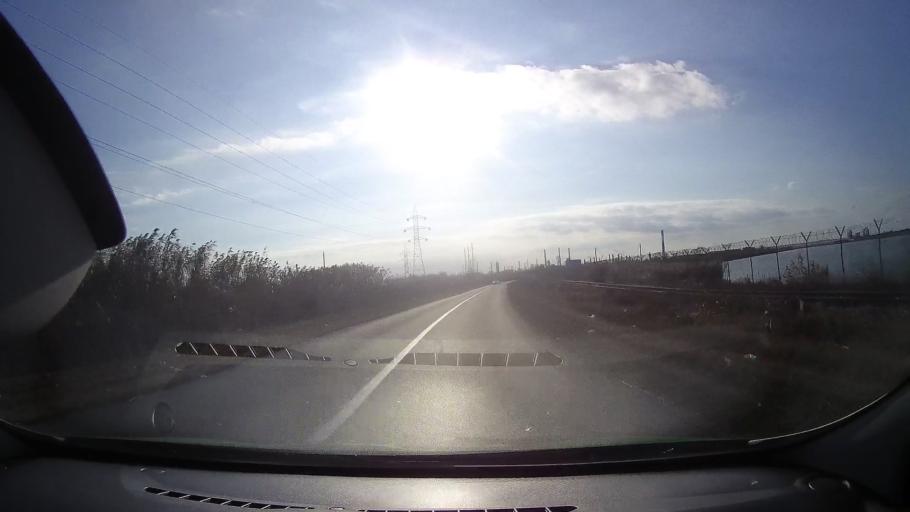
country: RO
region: Constanta
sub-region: Comuna Corbu
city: Corbu
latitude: 44.3565
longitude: 28.6749
